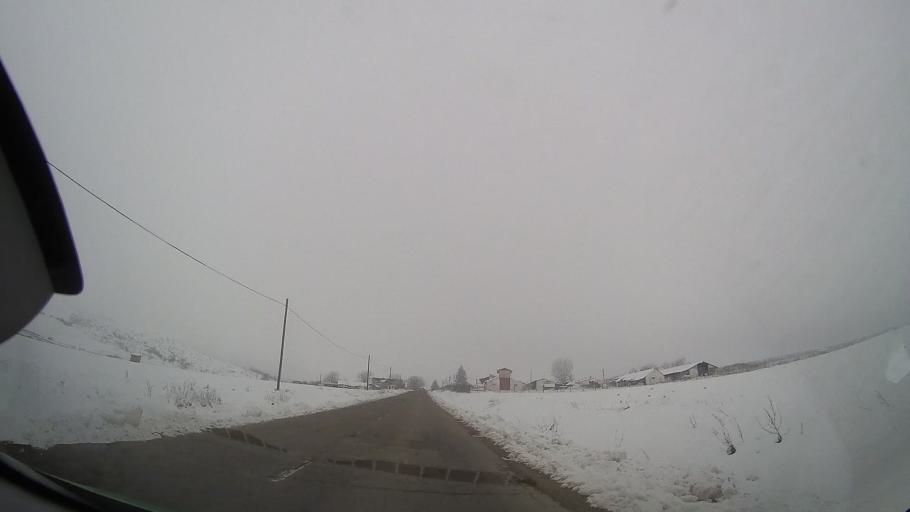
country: RO
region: Neamt
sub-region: Comuna Icusesti
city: Balusesti
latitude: 46.8562
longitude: 27.0300
